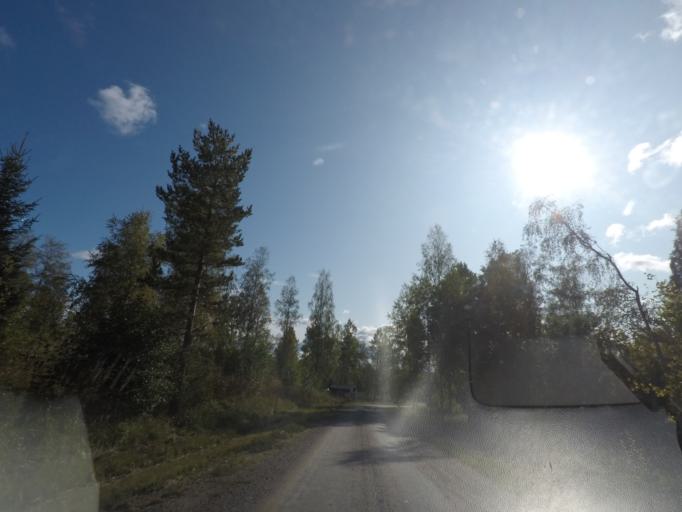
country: SE
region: Vaestmanland
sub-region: Skinnskattebergs Kommun
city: Skinnskatteberg
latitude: 59.8275
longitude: 15.5218
